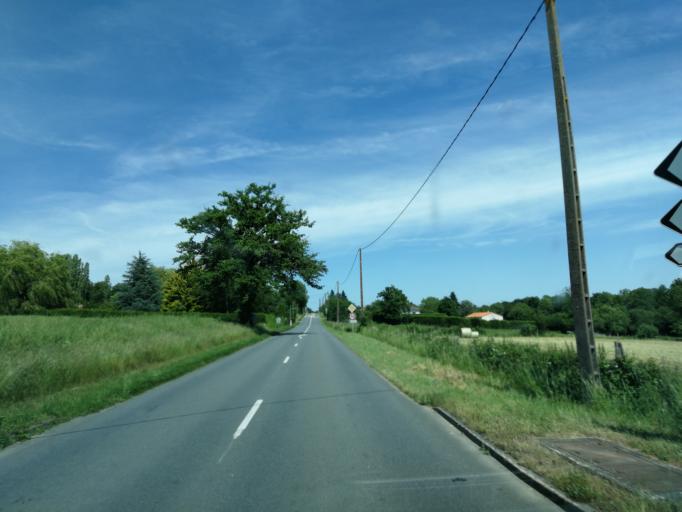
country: FR
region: Poitou-Charentes
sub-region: Departement des Deux-Sevres
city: Courlay
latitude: 46.7892
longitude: -0.6093
